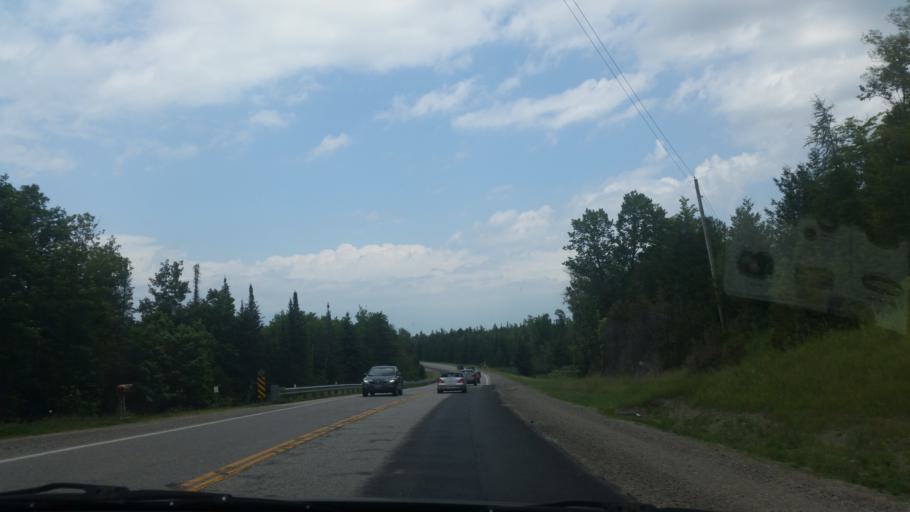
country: CA
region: Ontario
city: Orangeville
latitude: 43.7310
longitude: -80.0964
